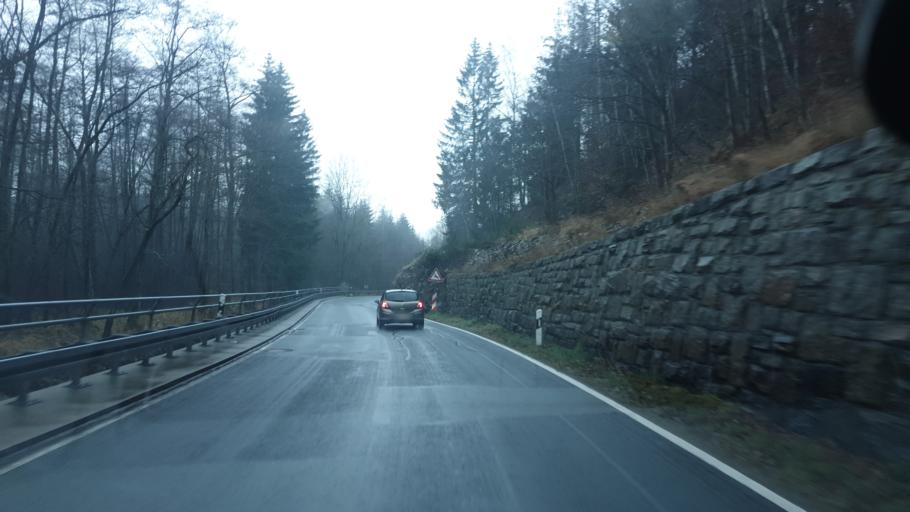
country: DE
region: Saxony
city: Seiffen
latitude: 50.6348
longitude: 13.4053
